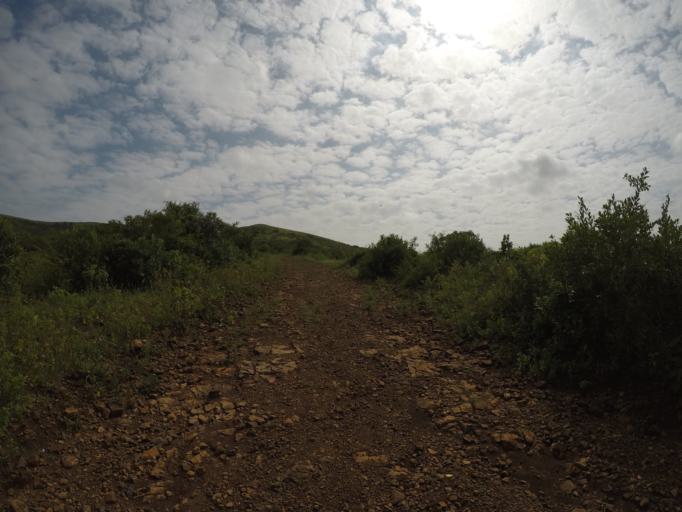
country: ZA
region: KwaZulu-Natal
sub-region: uThungulu District Municipality
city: Empangeni
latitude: -28.6137
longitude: 31.9047
